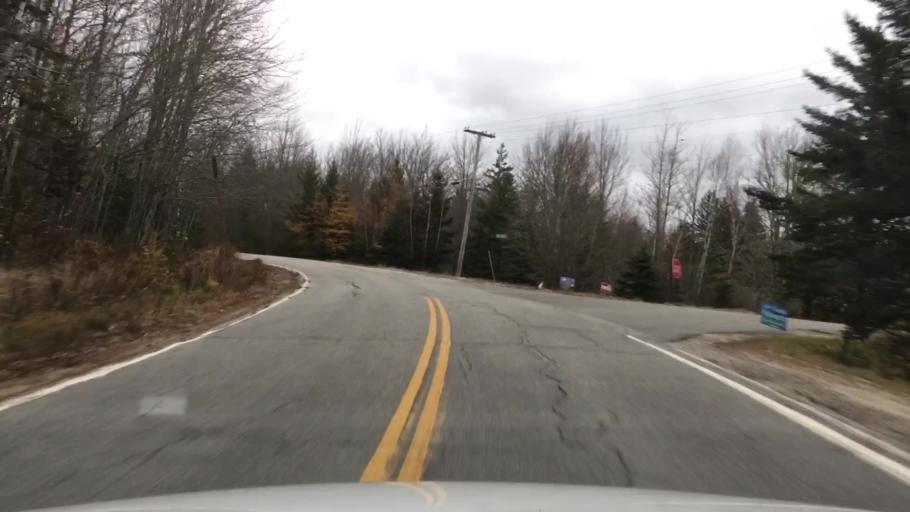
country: US
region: Maine
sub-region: Hancock County
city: Sedgwick
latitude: 44.2773
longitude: -68.5541
